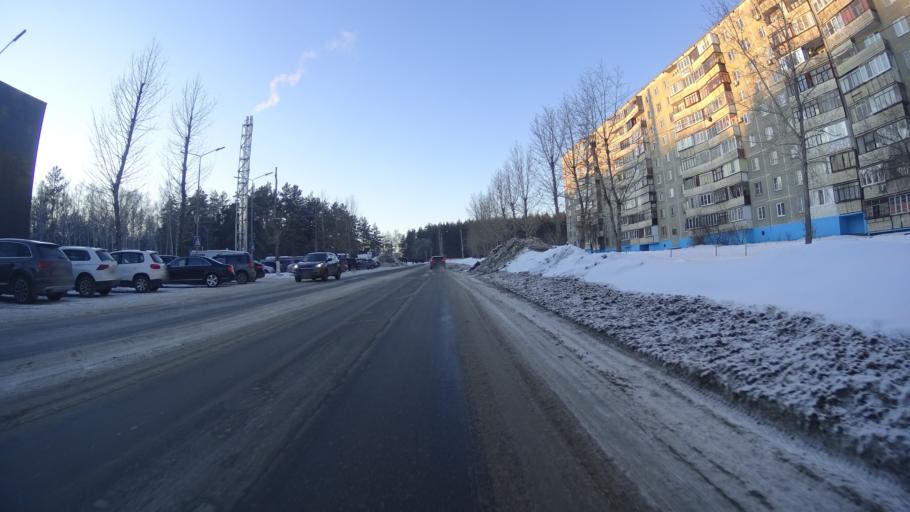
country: RU
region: Chelyabinsk
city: Roshchino
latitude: 55.1956
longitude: 61.2992
